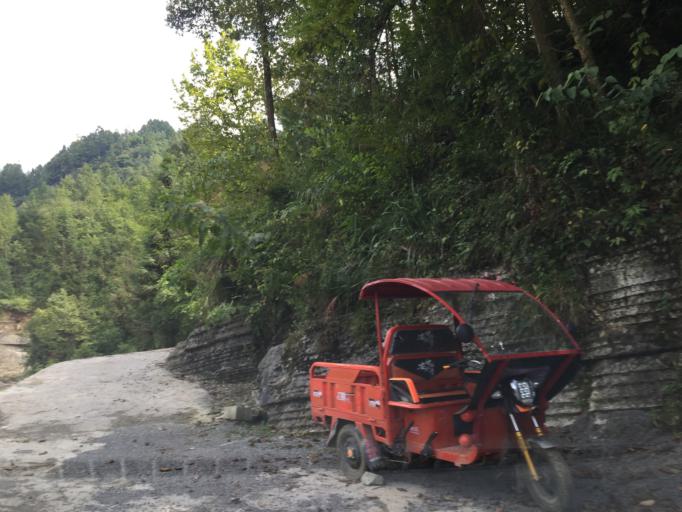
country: CN
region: Guizhou Sheng
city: Quankou
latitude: 28.5345
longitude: 108.1149
